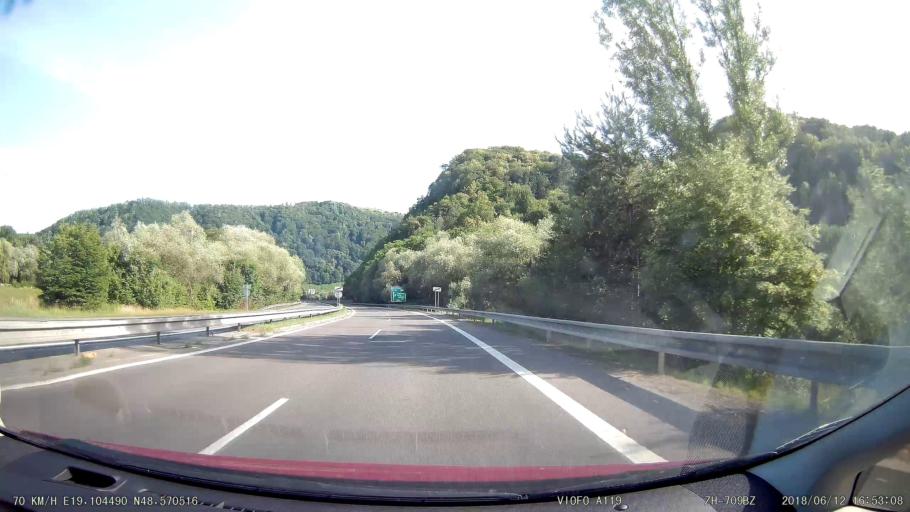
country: SK
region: Banskobystricky
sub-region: Okres Banska Bystrica
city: Zvolen
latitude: 48.5701
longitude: 19.1046
